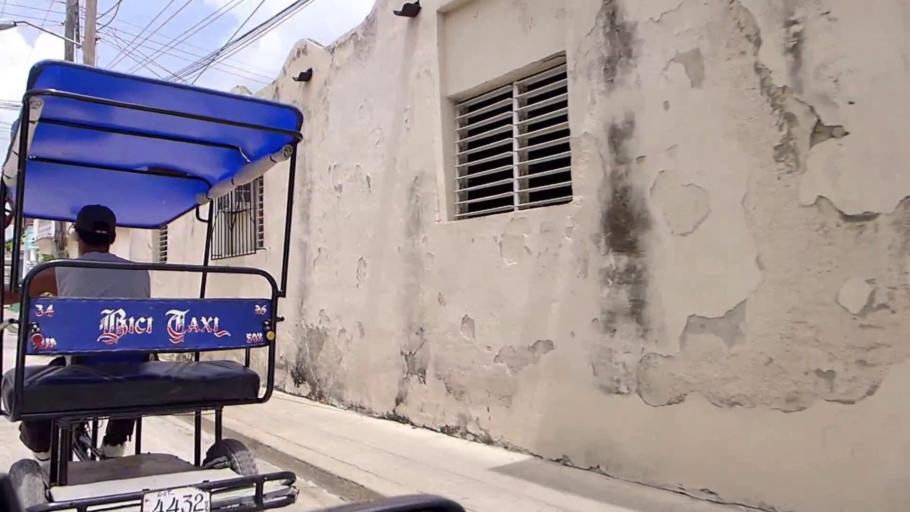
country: CU
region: Holguin
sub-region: Municipio de Holguin
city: Holguin
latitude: 20.8915
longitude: -76.2593
